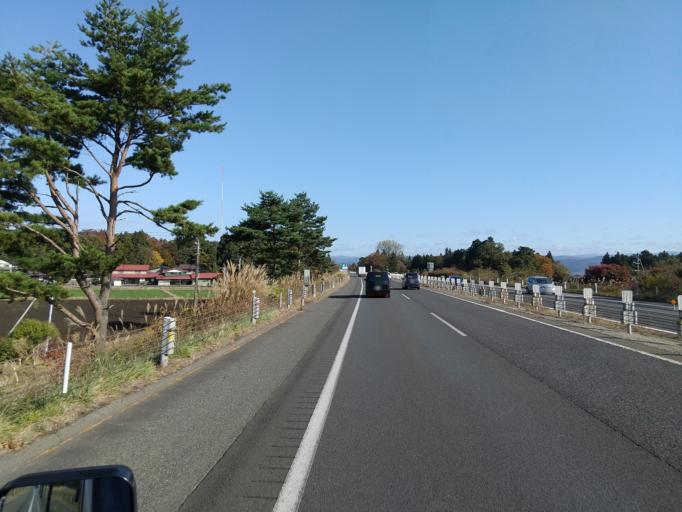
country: JP
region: Iwate
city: Morioka-shi
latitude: 39.6073
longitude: 141.1258
